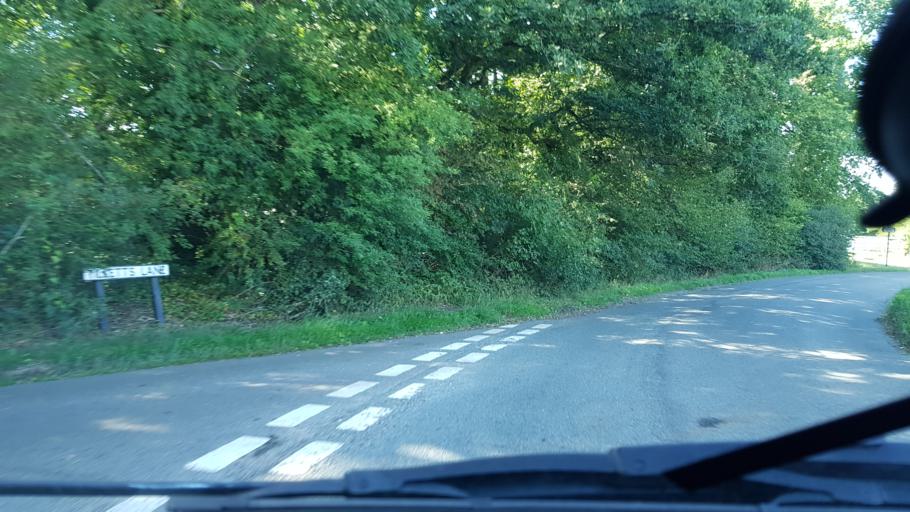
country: GB
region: England
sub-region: West Sussex
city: Horsham
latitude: 51.0953
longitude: -0.3528
